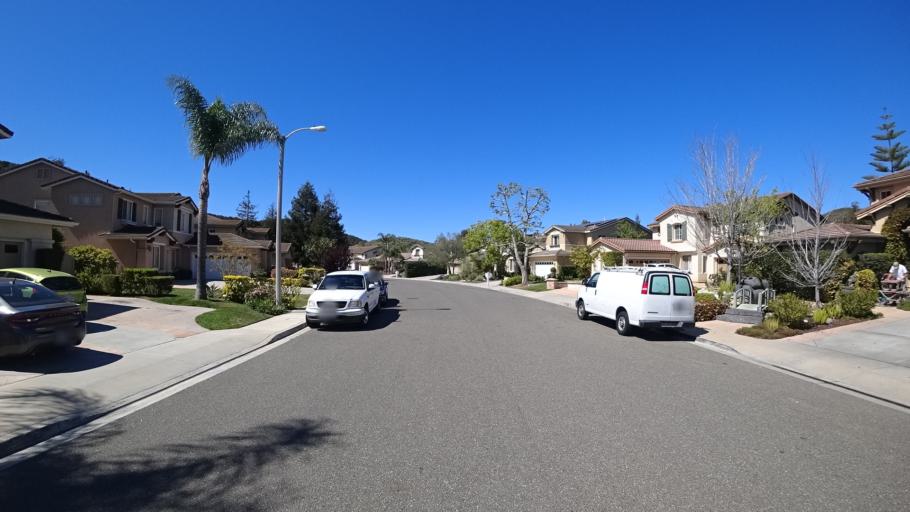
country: US
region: California
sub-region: Ventura County
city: Casa Conejo
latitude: 34.1670
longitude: -118.9761
